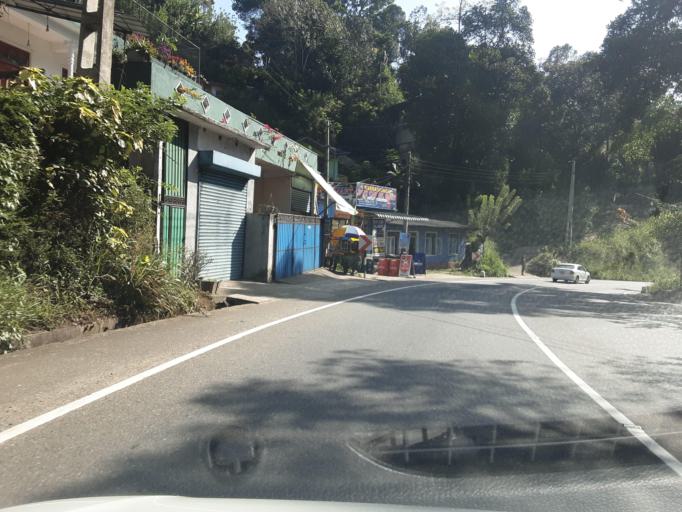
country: LK
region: Uva
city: Badulla
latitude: 6.9752
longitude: 81.0427
